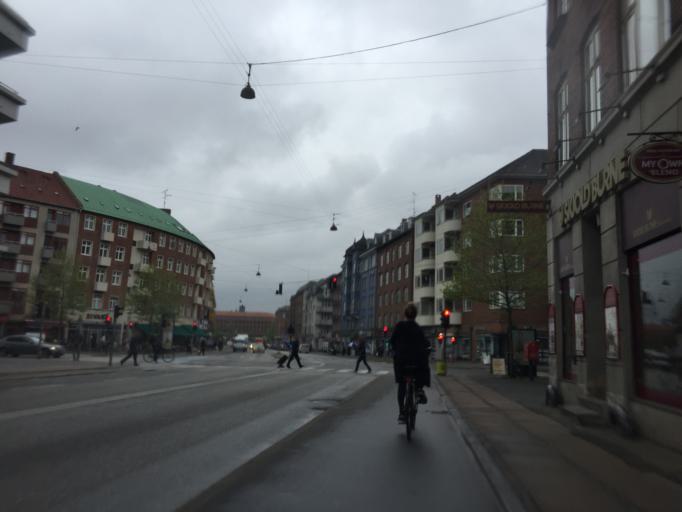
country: DK
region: Capital Region
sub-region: Frederiksberg Kommune
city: Frederiksberg
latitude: 55.7021
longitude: 12.5326
